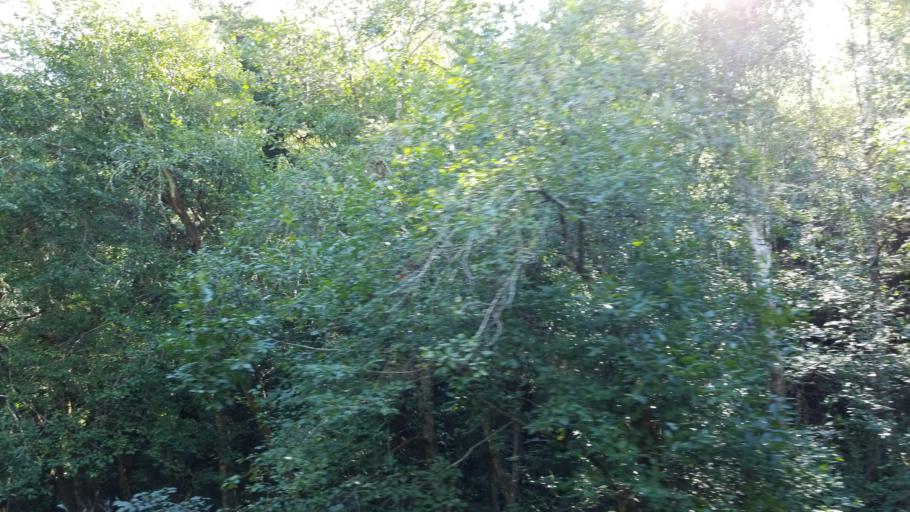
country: US
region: California
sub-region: Mendocino County
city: Fort Bragg
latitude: 39.4487
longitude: -123.7788
